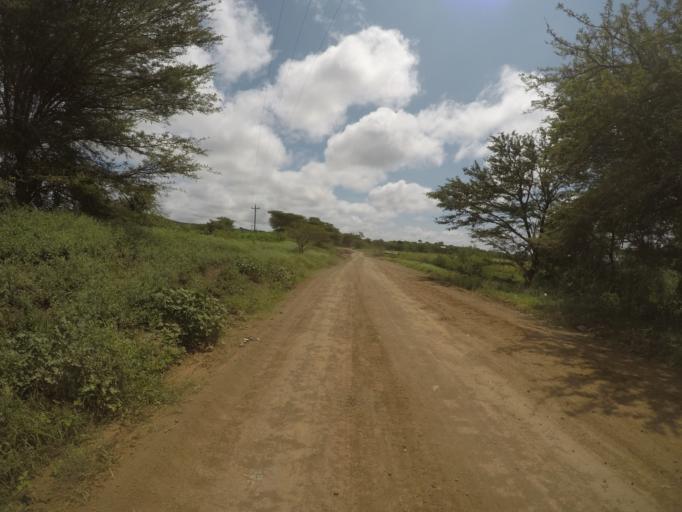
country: ZA
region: KwaZulu-Natal
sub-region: uThungulu District Municipality
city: Empangeni
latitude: -28.5714
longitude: 31.8371
